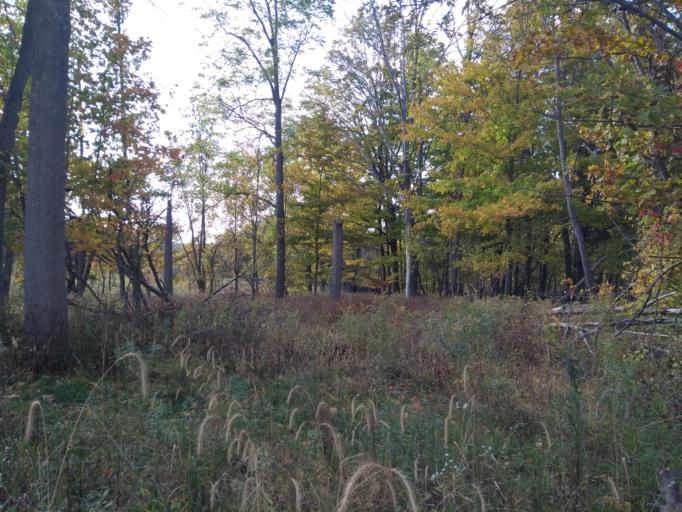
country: CA
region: Ontario
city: Thorold
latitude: 43.0965
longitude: -79.2776
